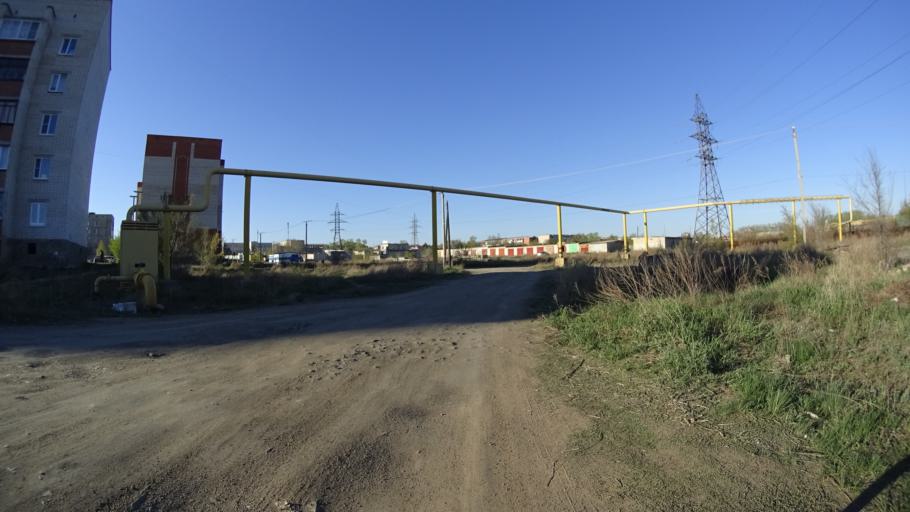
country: RU
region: Chelyabinsk
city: Troitsk
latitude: 54.0719
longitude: 61.5346
